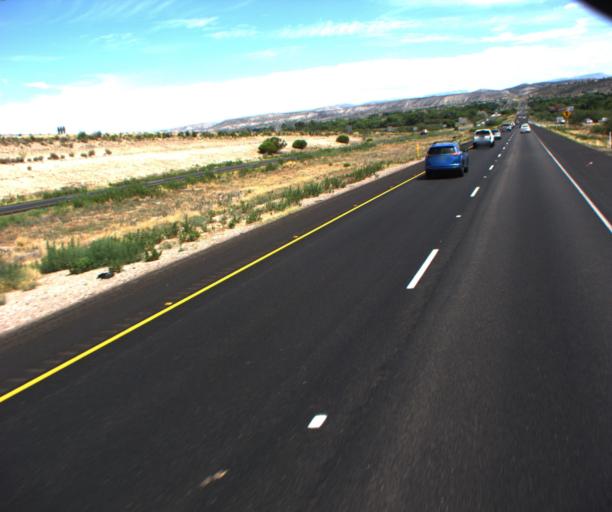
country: US
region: Arizona
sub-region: Yavapai County
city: Camp Verde
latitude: 34.5789
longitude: -111.8834
